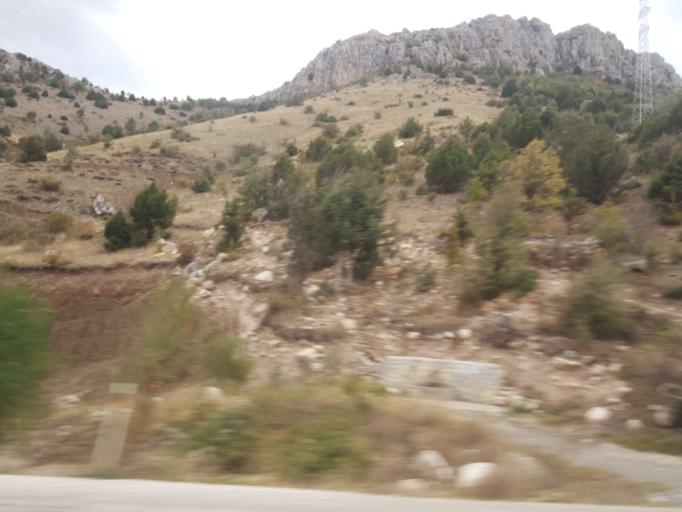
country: TR
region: Yozgat
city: Cekerek
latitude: 40.2110
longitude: 35.4942
